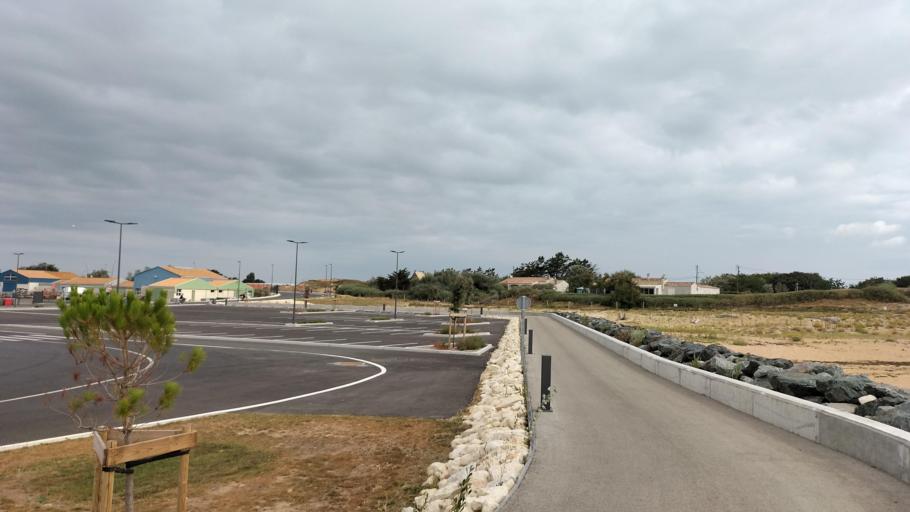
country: FR
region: Poitou-Charentes
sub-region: Departement de la Charente-Maritime
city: Dolus-d'Oleron
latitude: 45.9122
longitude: -1.3235
